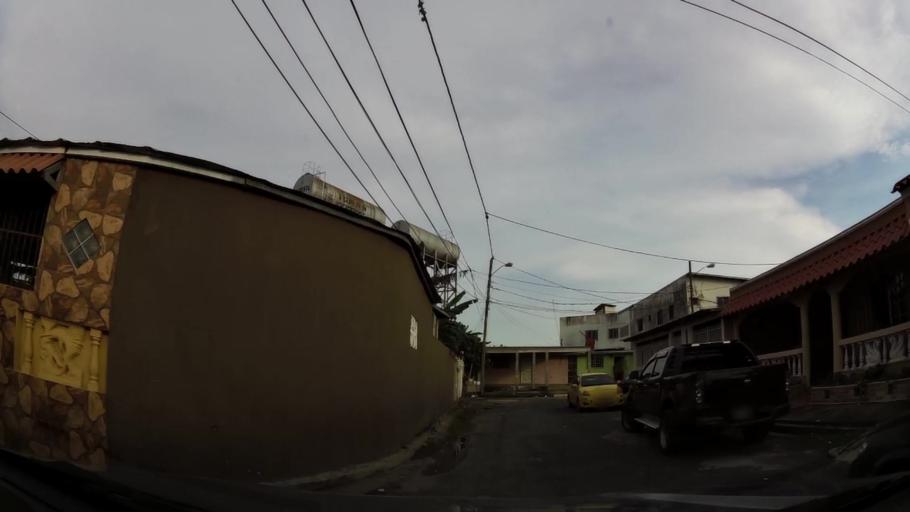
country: PA
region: Panama
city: Tocumen
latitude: 9.0779
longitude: -79.3645
